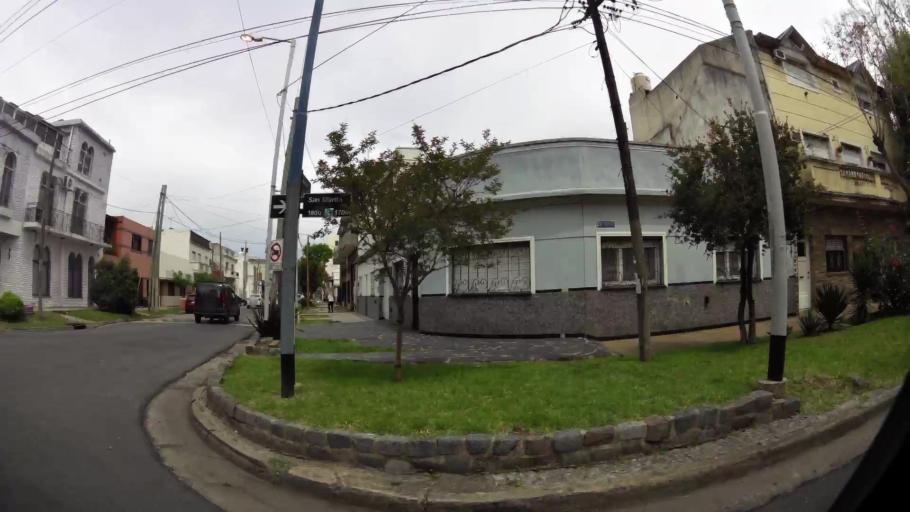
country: AR
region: Buenos Aires
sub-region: Partido de Avellaneda
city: Avellaneda
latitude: -34.6705
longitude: -58.3586
